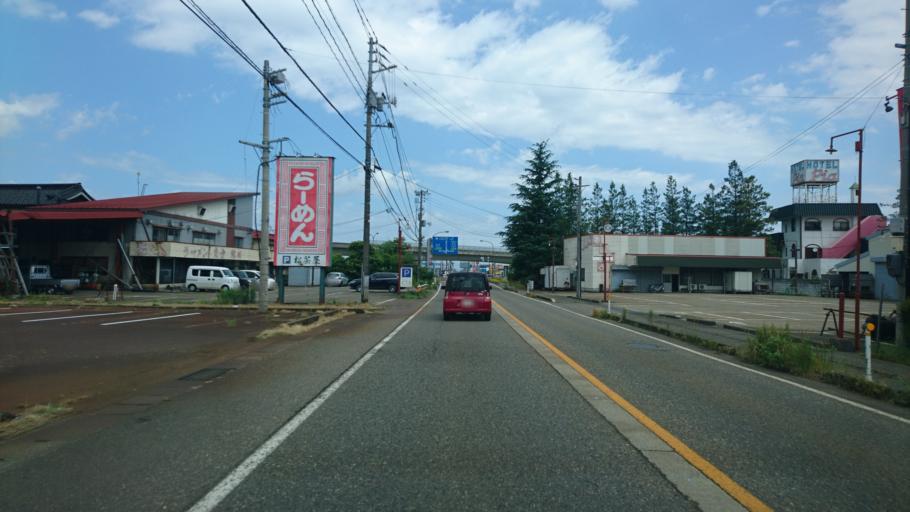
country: JP
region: Niigata
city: Arai
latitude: 37.0582
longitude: 138.2599
